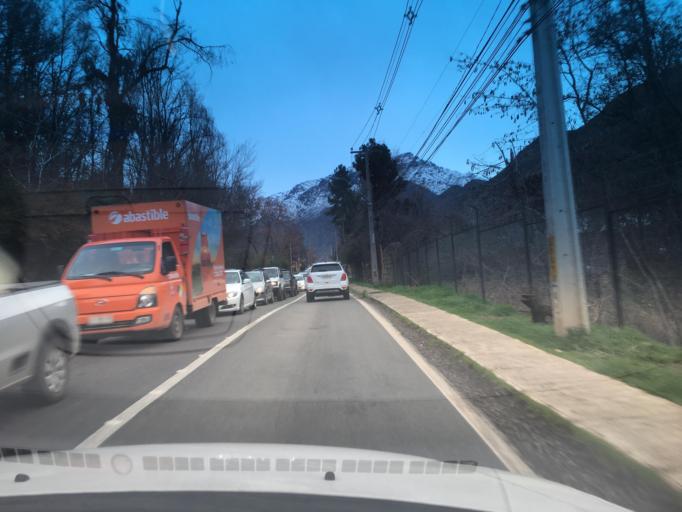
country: CL
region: Santiago Metropolitan
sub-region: Provincia de Cordillera
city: Puente Alto
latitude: -33.6885
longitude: -70.3359
